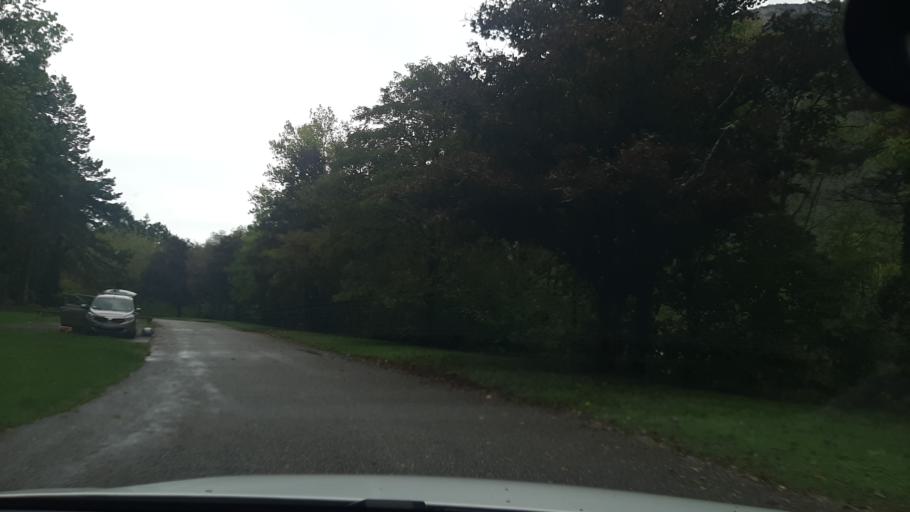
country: FR
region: Rhone-Alpes
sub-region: Departement de la Savoie
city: Montmelian
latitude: 45.5011
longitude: 6.0559
